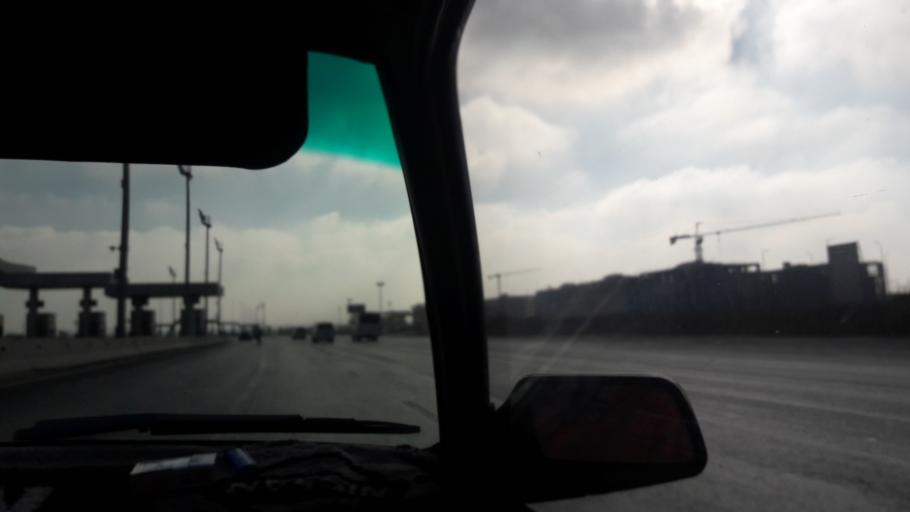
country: EG
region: Eastern Province
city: Bilbays
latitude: 30.2060
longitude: 31.6700
